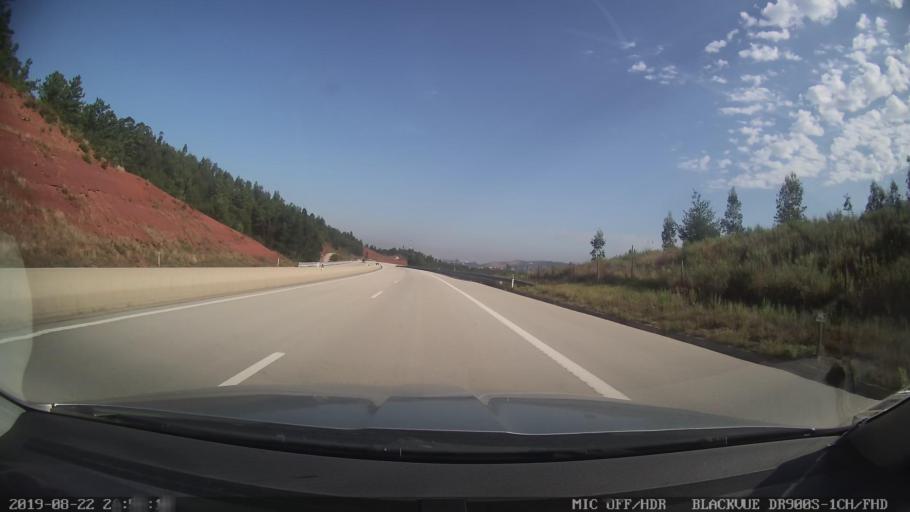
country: PT
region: Coimbra
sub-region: Coimbra
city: Coimbra
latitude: 40.1486
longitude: -8.3834
